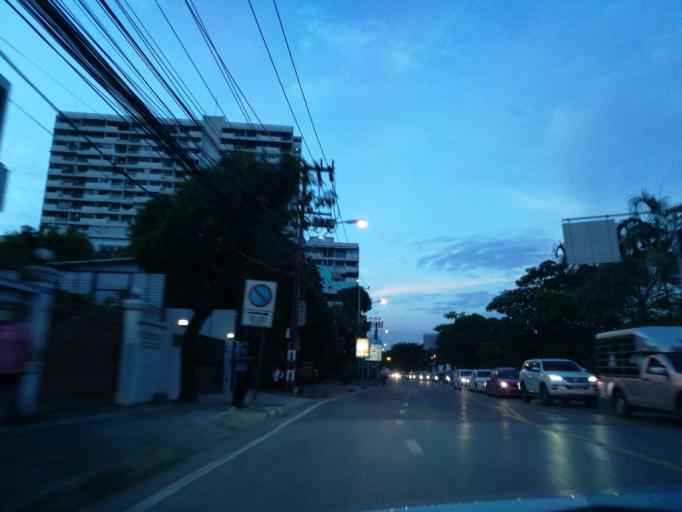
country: TH
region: Bangkok
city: Dusit
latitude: 13.7767
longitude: 100.5287
